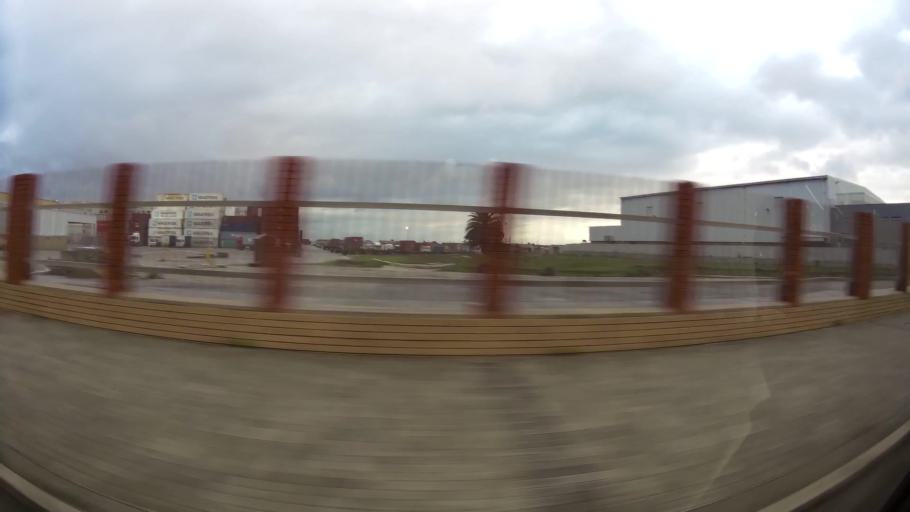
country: ZA
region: Eastern Cape
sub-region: Nelson Mandela Bay Metropolitan Municipality
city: Port Elizabeth
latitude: -33.9254
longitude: 25.5973
